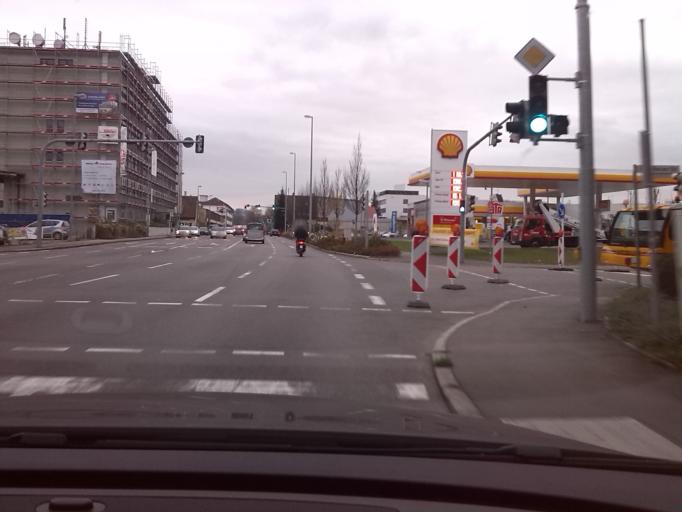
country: DE
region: Baden-Wuerttemberg
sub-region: Regierungsbezirk Stuttgart
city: Fellbach
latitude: 48.8152
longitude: 9.2597
